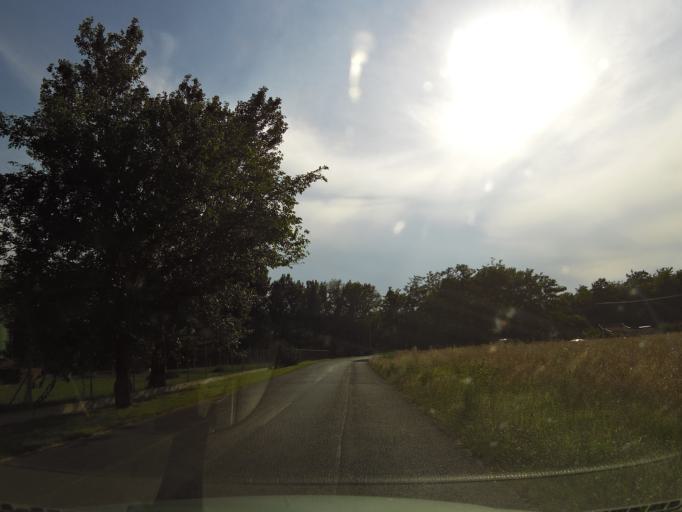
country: HU
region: Csongrad
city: Balastya
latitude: 46.4345
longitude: 19.9848
